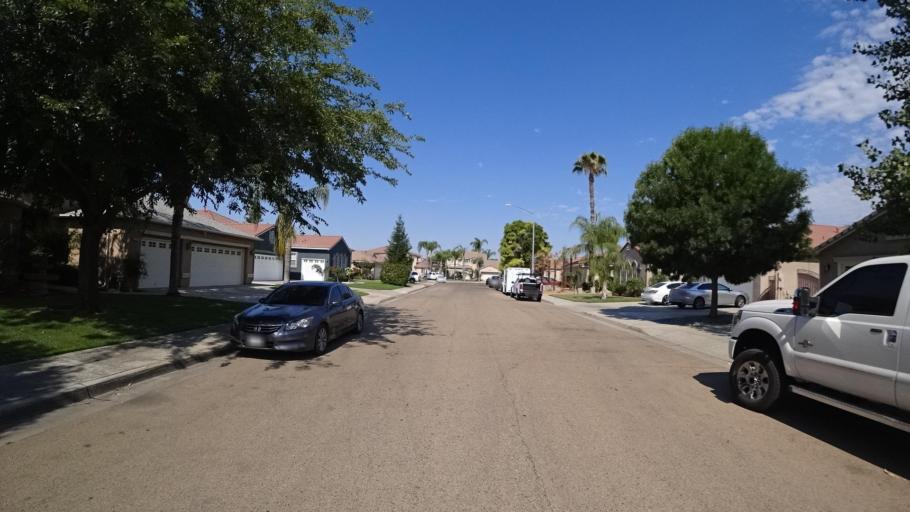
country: US
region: California
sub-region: Fresno County
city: Sunnyside
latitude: 36.7186
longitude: -119.6930
